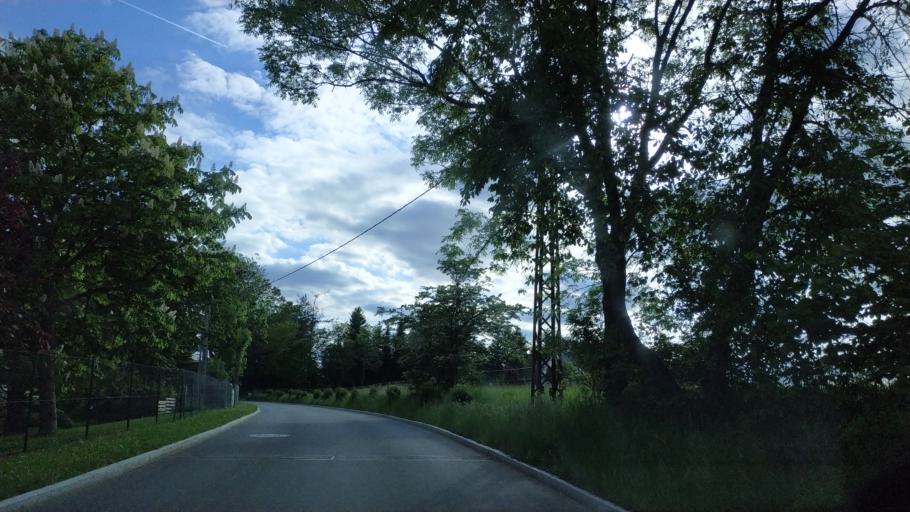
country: DE
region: Saxony
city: Pohl
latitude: 50.5485
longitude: 12.1493
